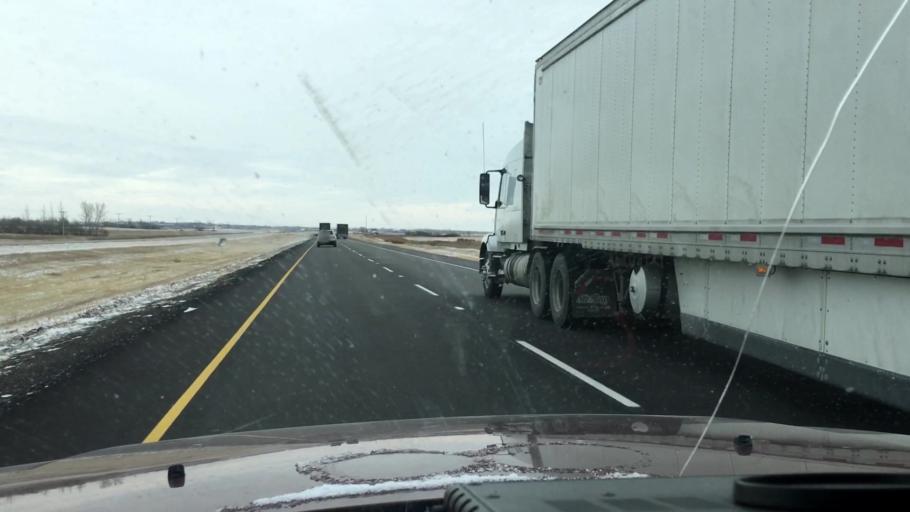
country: CA
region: Saskatchewan
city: Saskatoon
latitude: 51.7889
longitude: -106.4824
